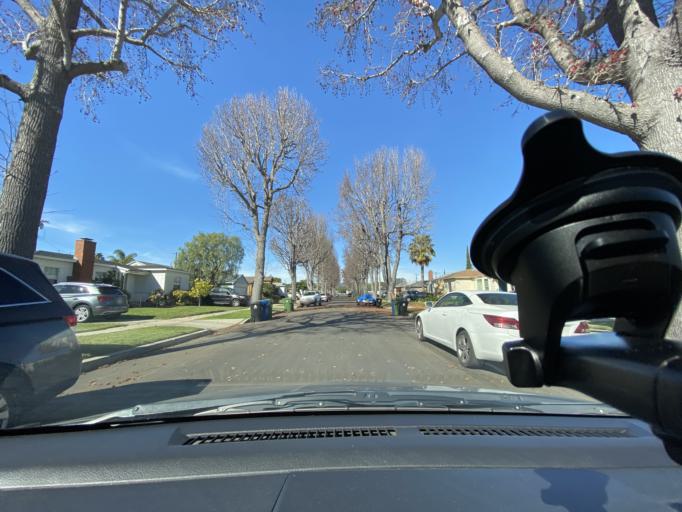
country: US
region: California
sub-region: Los Angeles County
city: Westwood, Los Angeles
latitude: 34.0251
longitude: -118.4373
